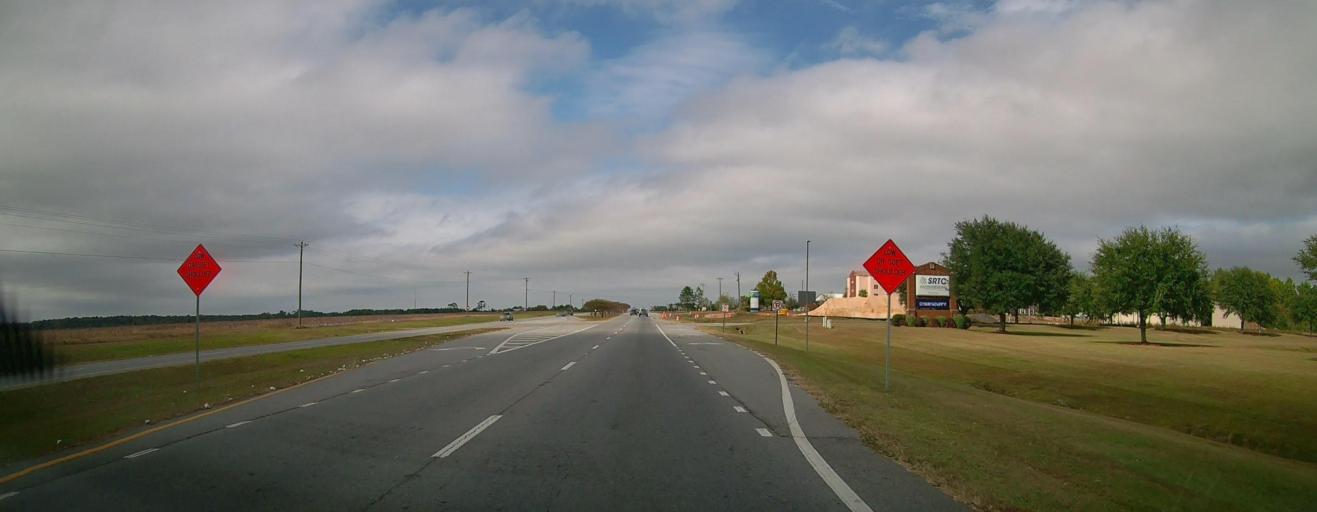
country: US
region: Georgia
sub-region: Colquitt County
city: Moultrie
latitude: 31.1966
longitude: -83.7678
